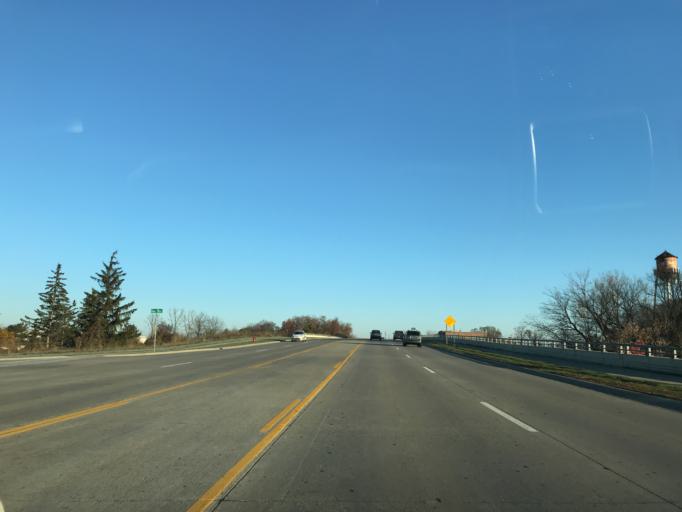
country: US
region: Michigan
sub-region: Oakland County
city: Novi
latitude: 42.4737
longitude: -83.4750
